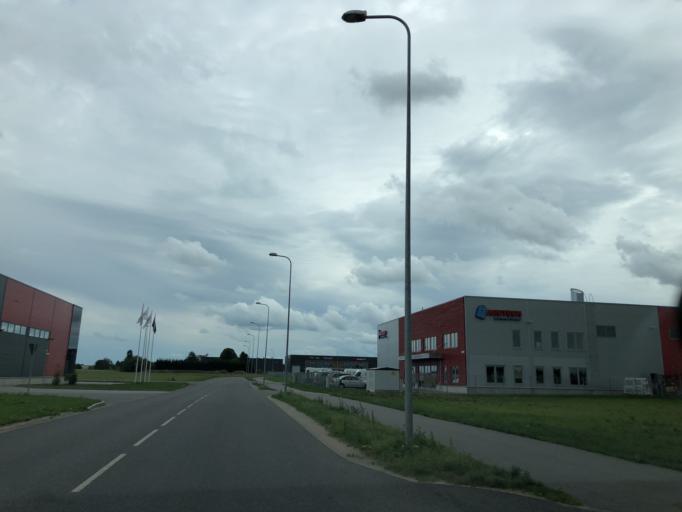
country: EE
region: Harju
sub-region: Rae vald
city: Jueri
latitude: 59.3910
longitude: 24.8231
